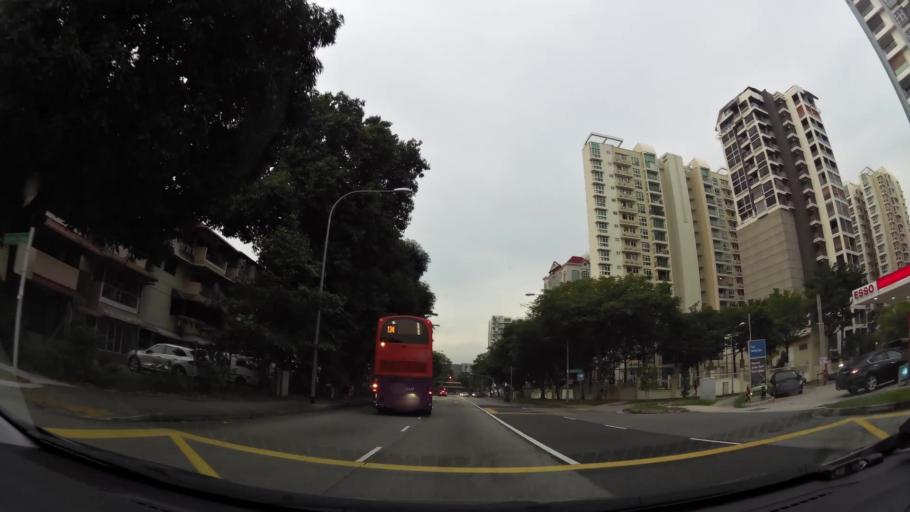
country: SG
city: Singapore
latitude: 1.3112
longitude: 103.8942
